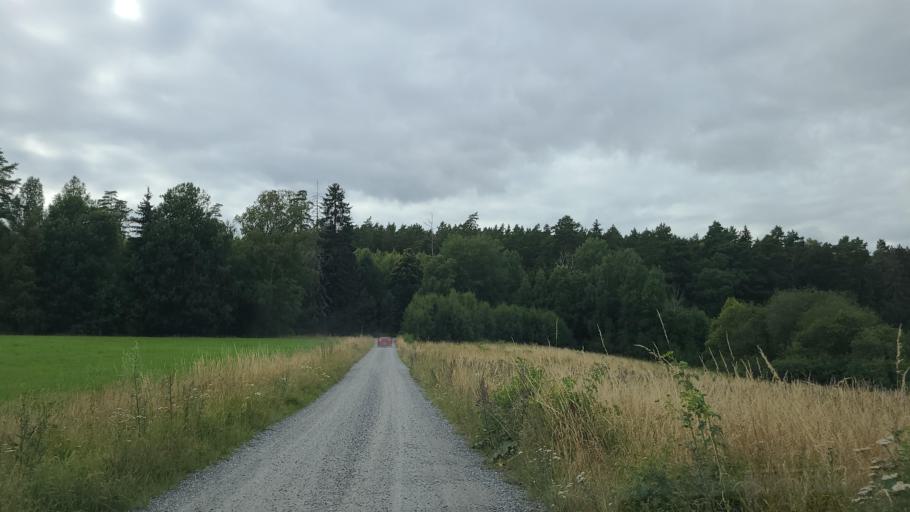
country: SE
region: Uppsala
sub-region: Habo Kommun
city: Balsta
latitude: 59.5121
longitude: 17.5594
